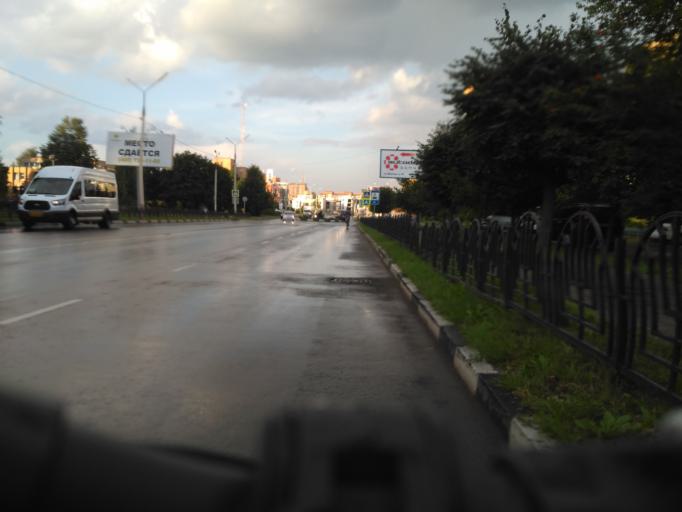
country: RU
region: Moskovskaya
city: Dubna
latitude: 56.7331
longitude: 37.1525
